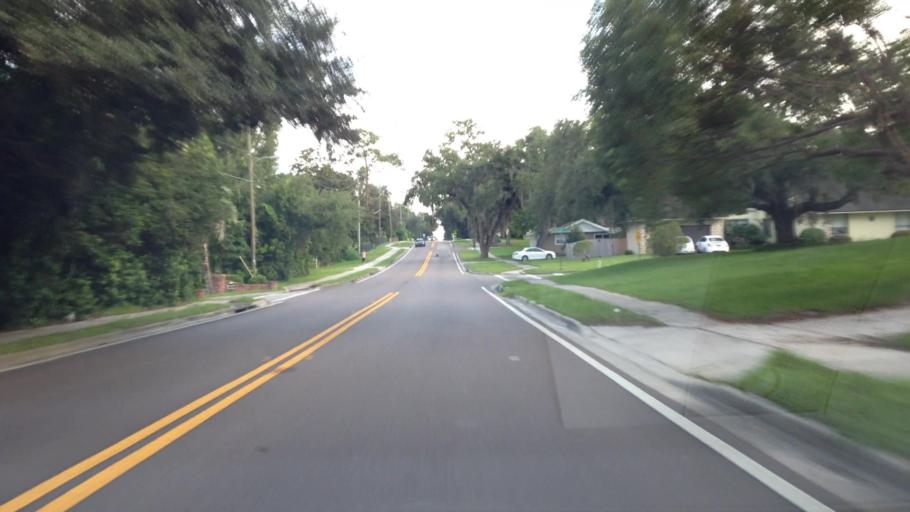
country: US
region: Florida
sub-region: Seminole County
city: Forest City
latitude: 28.6644
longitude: -81.4439
